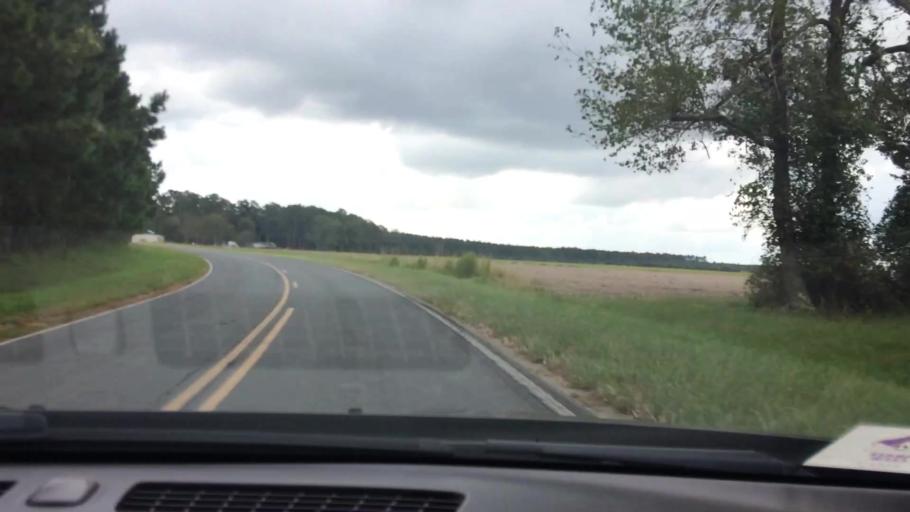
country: US
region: North Carolina
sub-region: Greene County
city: Maury
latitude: 35.5235
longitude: -77.5423
